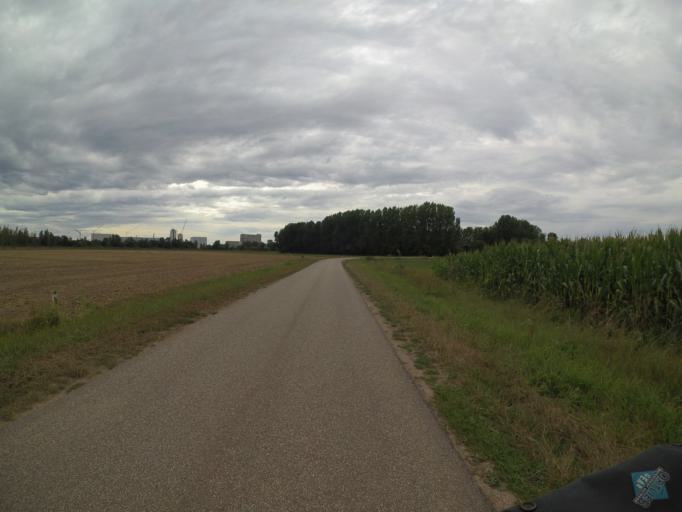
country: NL
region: North Brabant
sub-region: Gemeente Oss
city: Berghem
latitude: 51.7975
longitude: 5.5484
